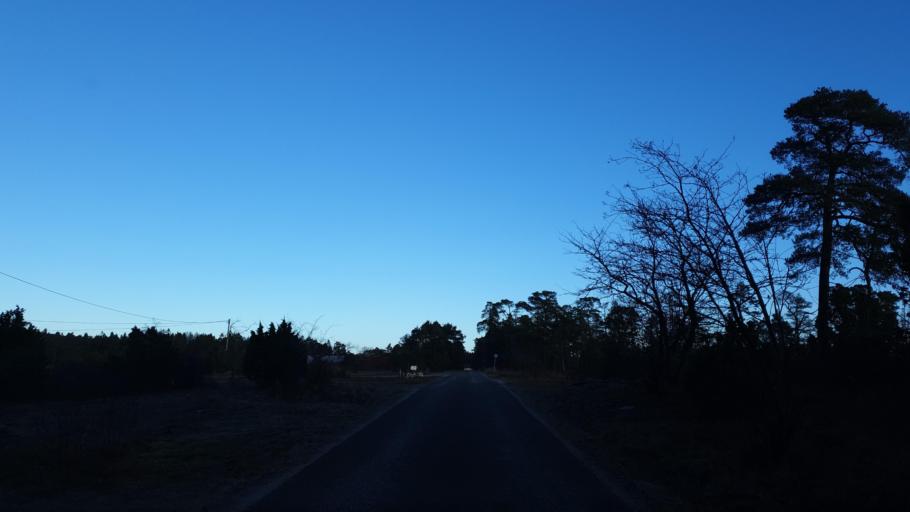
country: SE
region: Gotland
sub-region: Gotland
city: Slite
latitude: 57.3790
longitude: 18.8043
